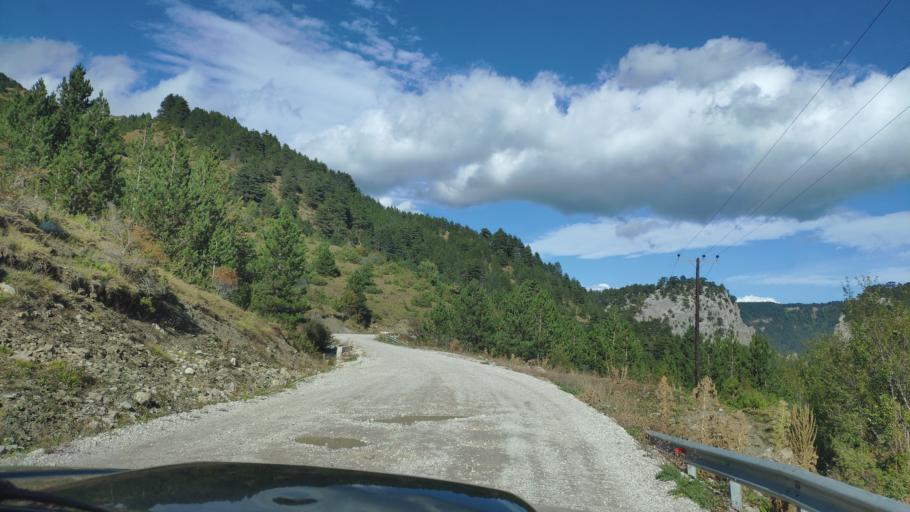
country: AL
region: Korce
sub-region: Rrethi i Devollit
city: Miras
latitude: 40.4029
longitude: 20.8539
